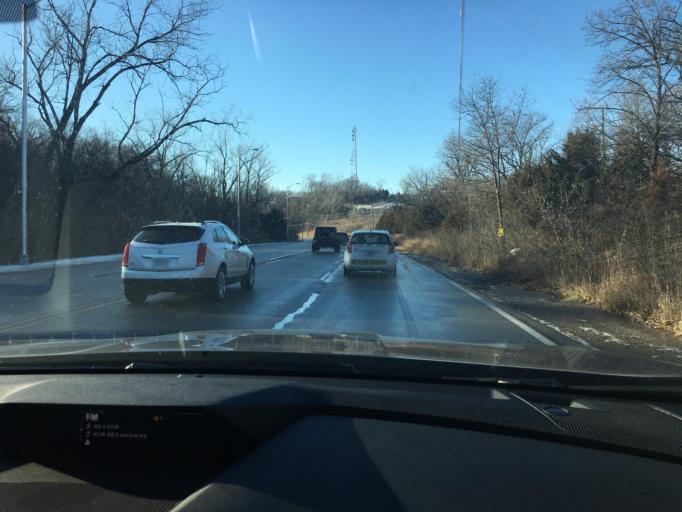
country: US
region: Missouri
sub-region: Jackson County
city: Raytown
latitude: 39.0132
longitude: -94.5003
